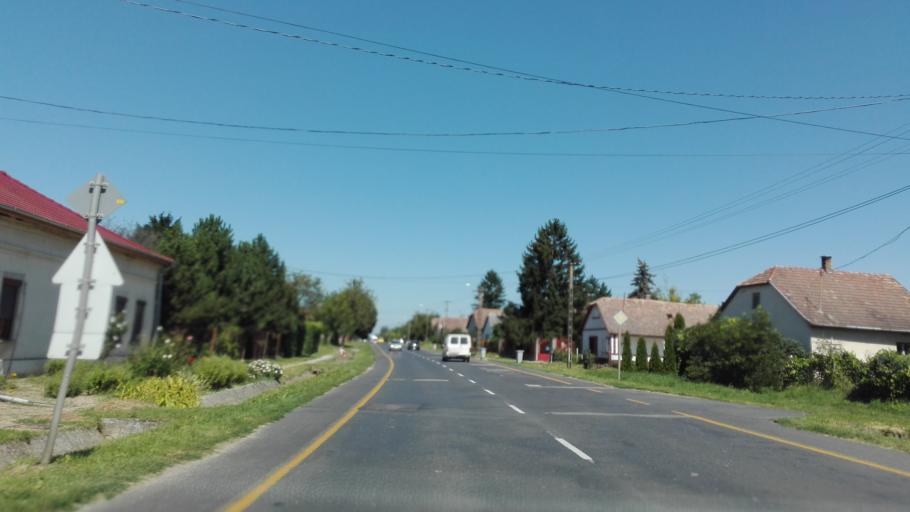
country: HU
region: Tolna
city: Simontornya
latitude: 46.7767
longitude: 18.5136
